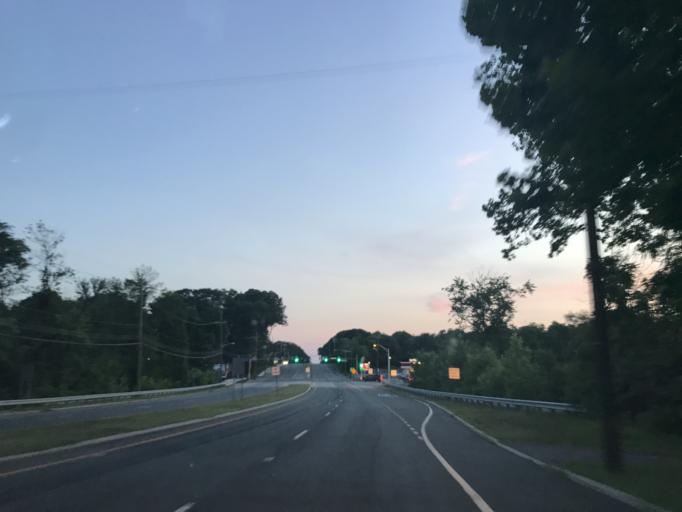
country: US
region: New Jersey
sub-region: Burlington County
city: Roebling
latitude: 40.1132
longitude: -74.7681
